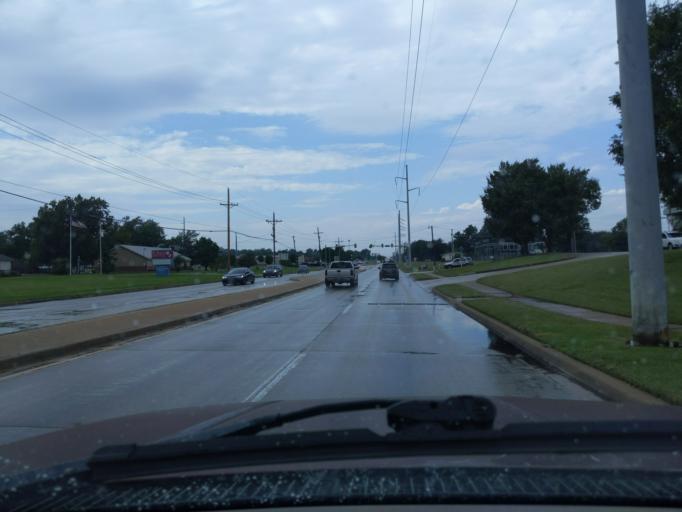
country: US
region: Oklahoma
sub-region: Tulsa County
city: Broken Arrow
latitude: 36.1336
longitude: -95.8735
